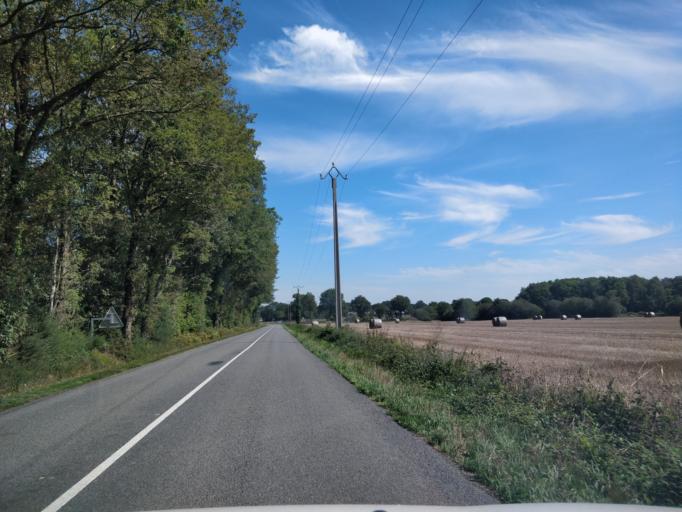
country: FR
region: Pays de la Loire
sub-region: Departement de la Loire-Atlantique
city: Conquereuil
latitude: 47.6581
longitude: -1.7823
